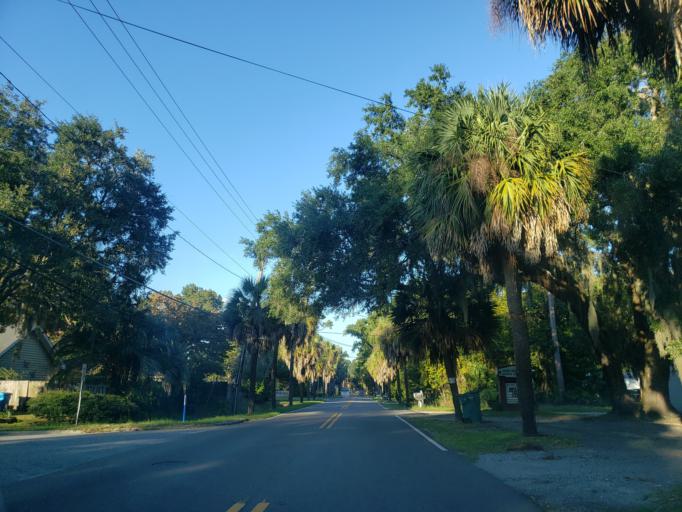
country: US
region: Georgia
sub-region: Chatham County
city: Isle of Hope
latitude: 31.9885
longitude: -81.0711
